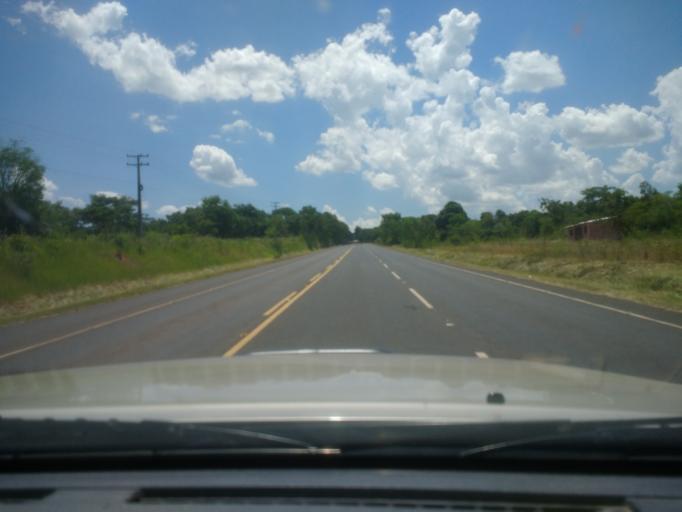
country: PY
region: San Pedro
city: Guayaybi
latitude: -24.5975
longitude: -56.5059
